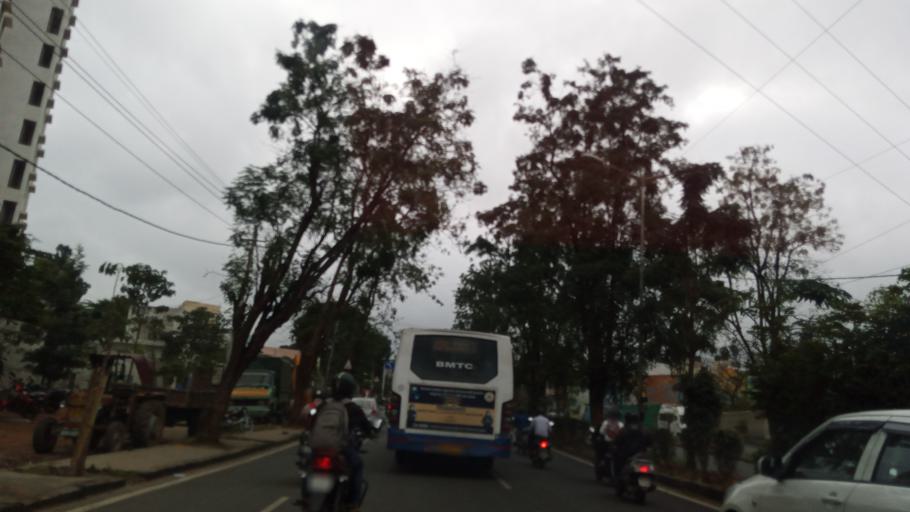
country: IN
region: Karnataka
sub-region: Bangalore Urban
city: Bangalore
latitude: 12.9359
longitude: 77.5355
